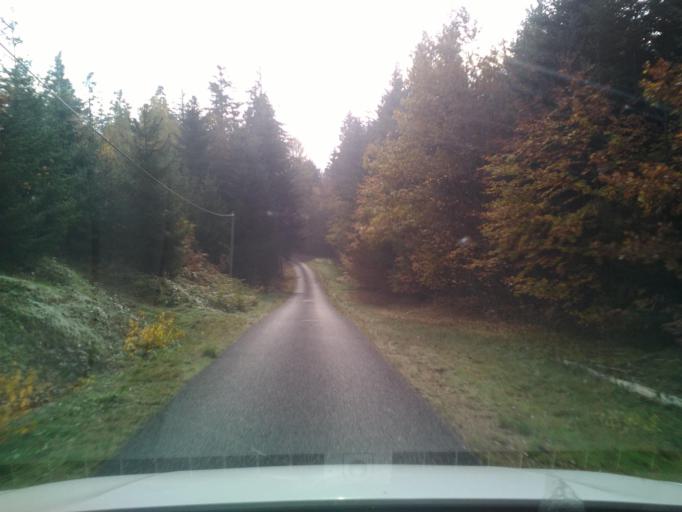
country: FR
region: Lorraine
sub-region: Departement des Vosges
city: Moyenmoutier
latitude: 48.3632
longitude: 6.8927
